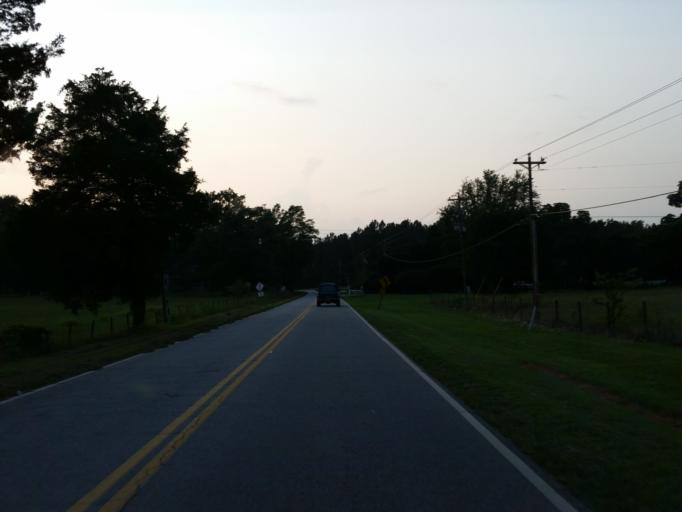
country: US
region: Georgia
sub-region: Spalding County
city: East Griffin
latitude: 33.2866
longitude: -84.1634
